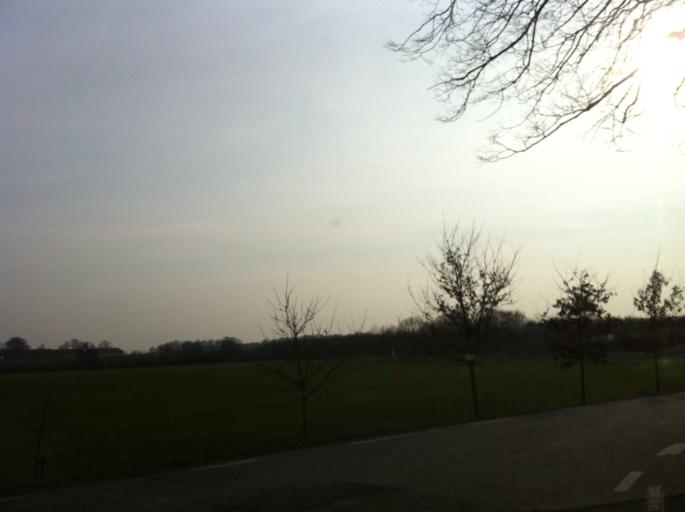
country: SE
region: Skane
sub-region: Eslovs Kommun
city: Eslov
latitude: 55.9395
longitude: 13.2791
